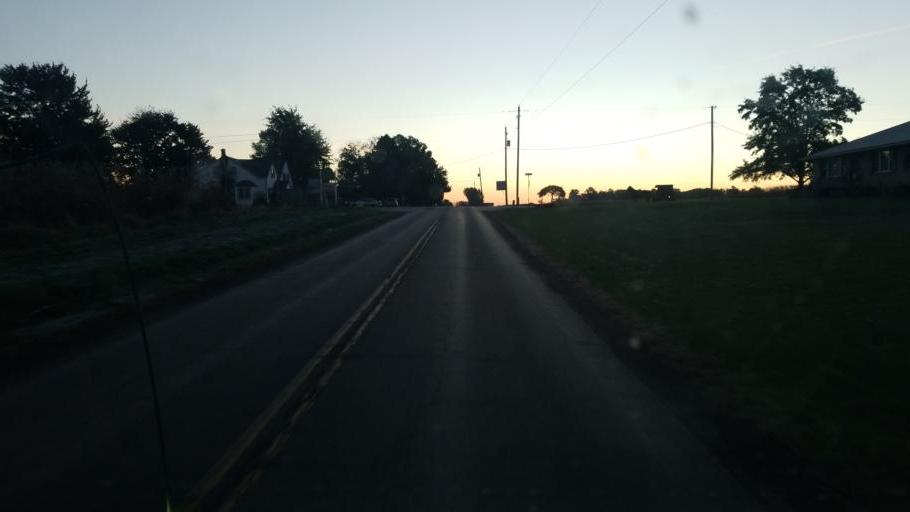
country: US
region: Ohio
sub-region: Wayne County
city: Apple Creek
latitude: 40.7412
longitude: -81.7761
